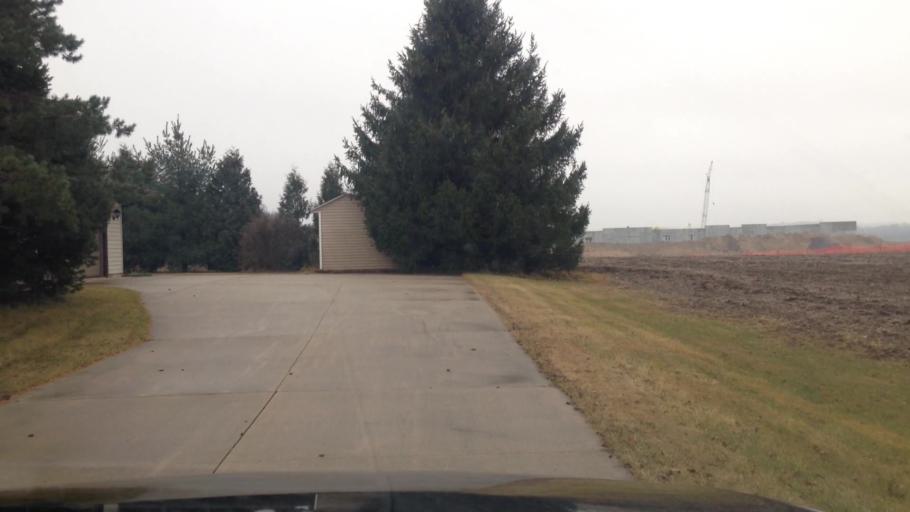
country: US
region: Wisconsin
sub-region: Washington County
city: Richfield
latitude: 43.2575
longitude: -88.1681
